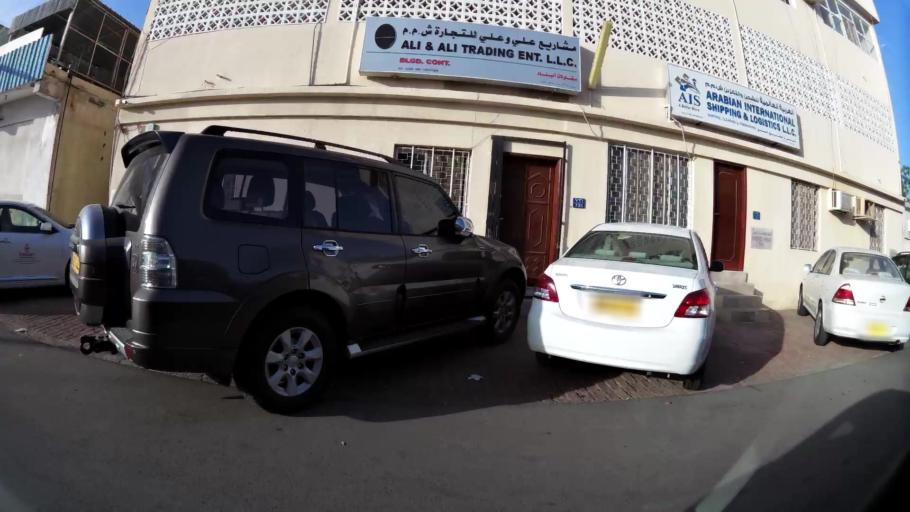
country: OM
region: Muhafazat Masqat
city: Muscat
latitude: 23.5880
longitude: 58.5553
